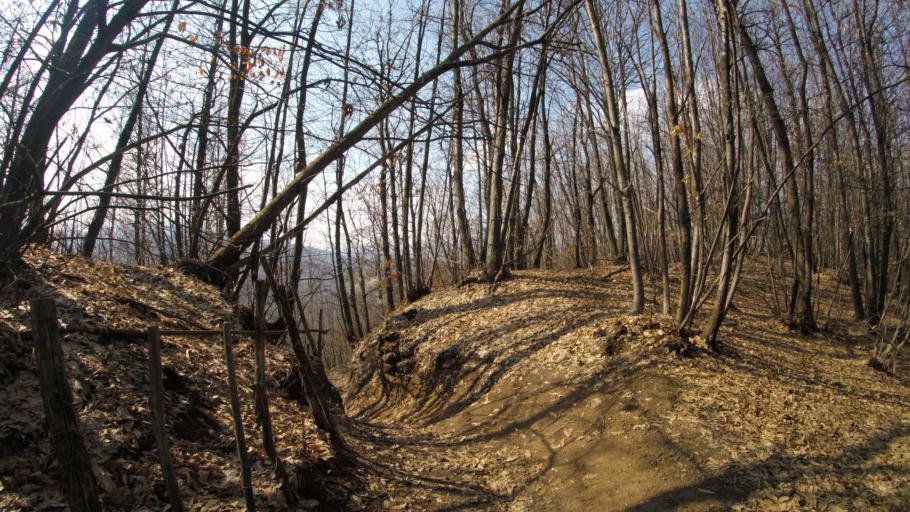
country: IT
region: Piedmont
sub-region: Provincia di Cuneo
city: Rossana
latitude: 44.5386
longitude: 7.4406
